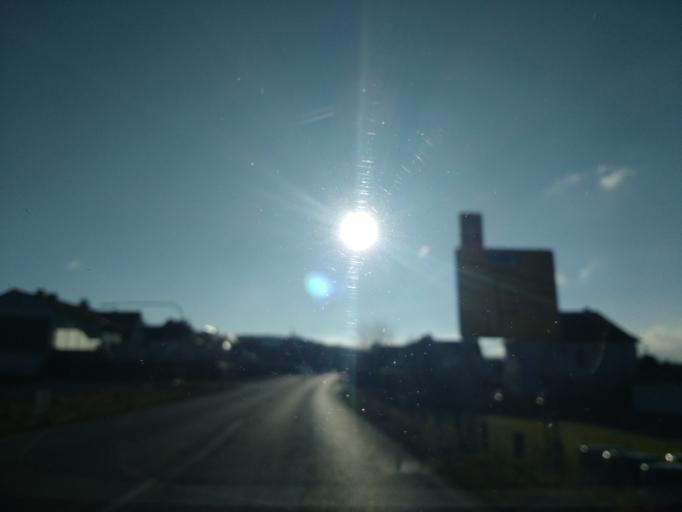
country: DE
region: Hesse
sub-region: Regierungsbezirk Kassel
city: Schrecksbach
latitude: 50.8573
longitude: 9.2908
